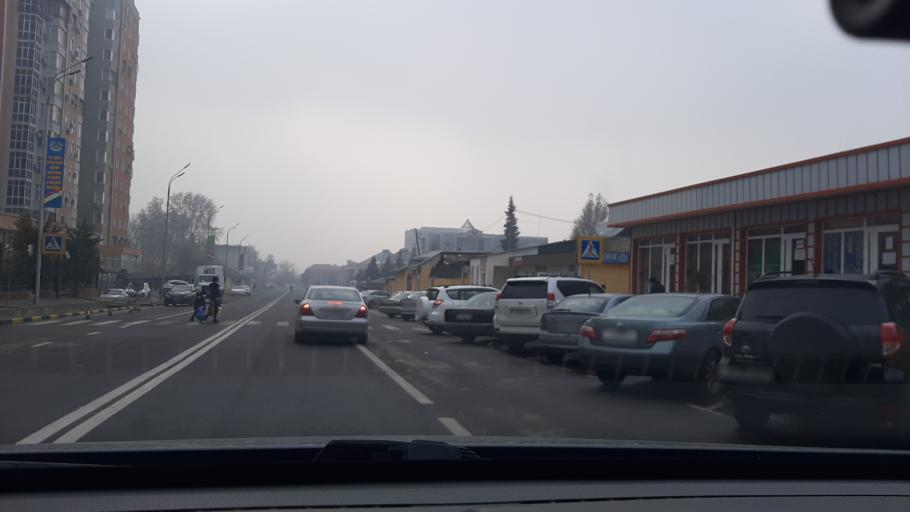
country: TJ
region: Dushanbe
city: Dushanbe
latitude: 38.5602
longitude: 68.7957
